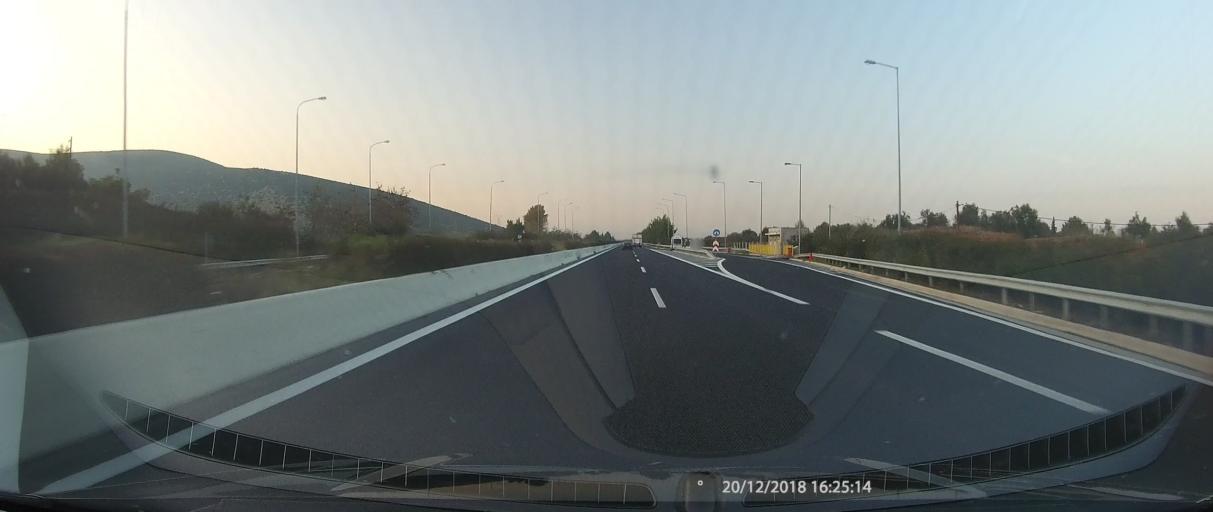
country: GR
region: Thessaly
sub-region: Nomos Magnisias
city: Sourpi
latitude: 39.1238
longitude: 22.8474
